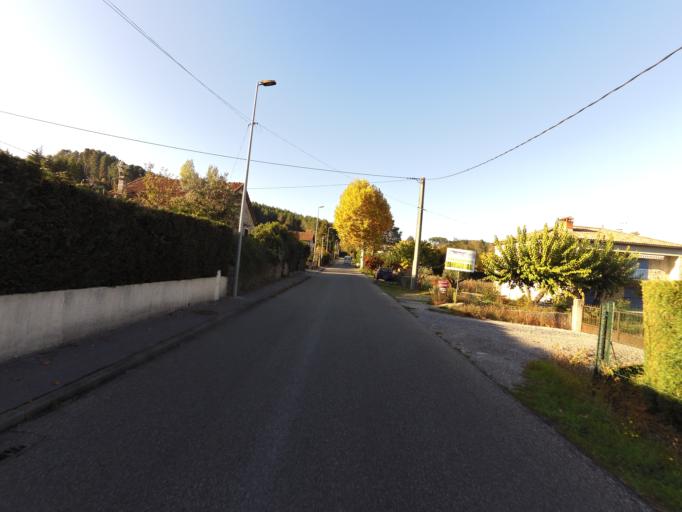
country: FR
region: Rhone-Alpes
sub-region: Departement de l'Ardeche
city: Joyeuse
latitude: 44.4828
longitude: 4.2307
